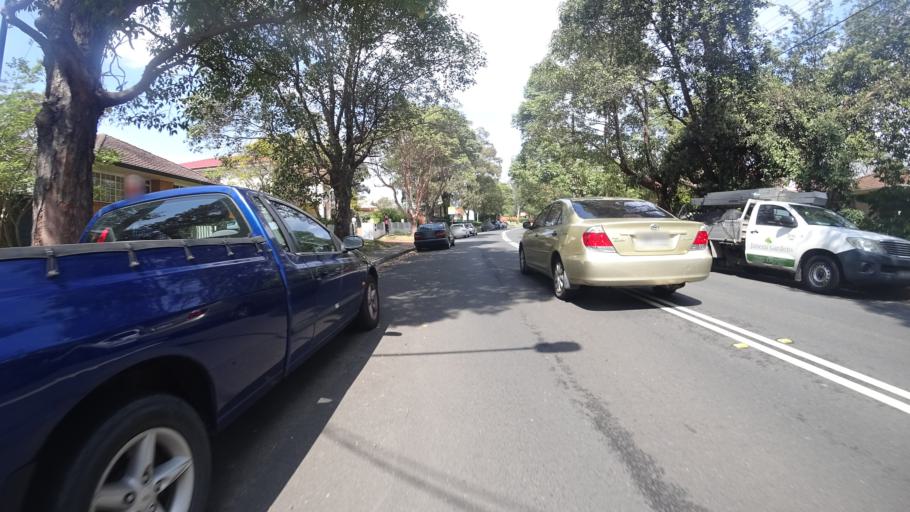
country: AU
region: New South Wales
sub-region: Hornsby Shire
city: Mount Colah
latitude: -33.6869
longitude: 151.1106
